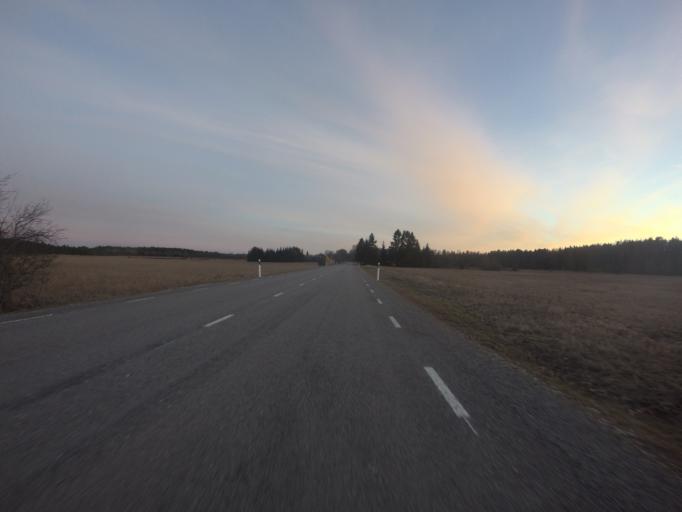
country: EE
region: Saare
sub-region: Orissaare vald
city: Orissaare
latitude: 58.5848
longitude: 22.7062
